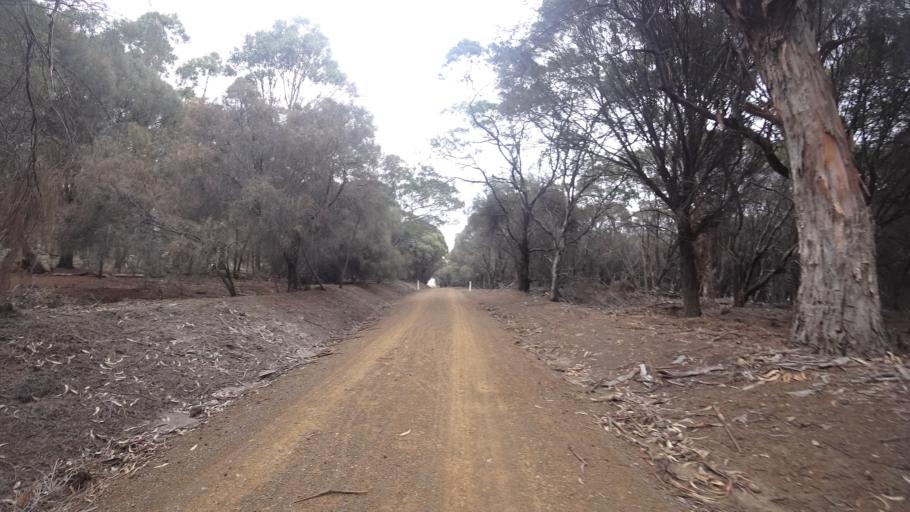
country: AU
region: Tasmania
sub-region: Sorell
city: Sorell
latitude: -42.5936
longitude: 148.0520
